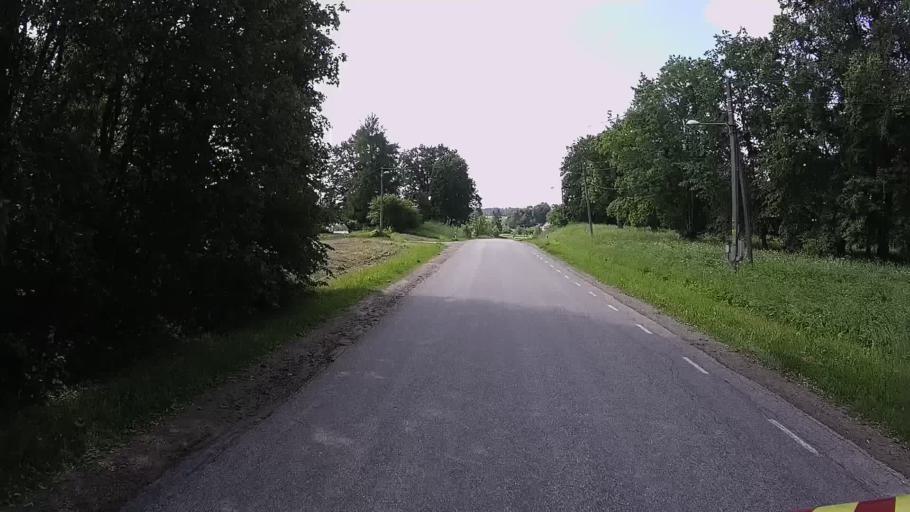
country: EE
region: Vorumaa
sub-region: Antsla vald
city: Vana-Antsla
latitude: 57.8634
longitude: 26.6086
